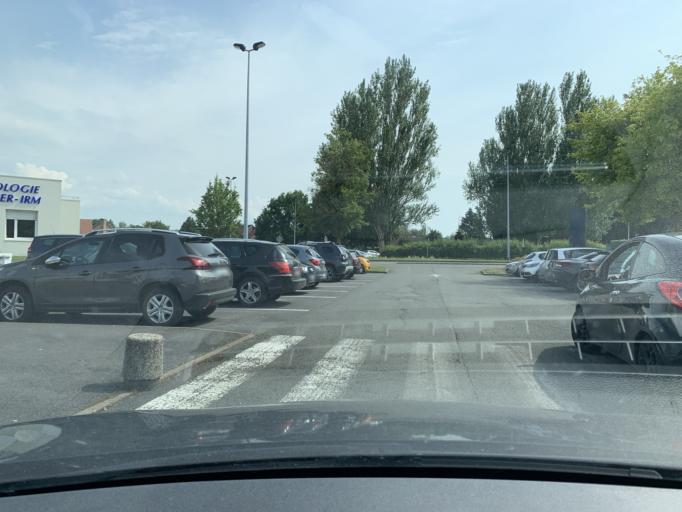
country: FR
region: Nord-Pas-de-Calais
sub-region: Departement du Nord
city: Douai
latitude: 50.3588
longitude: 3.0573
